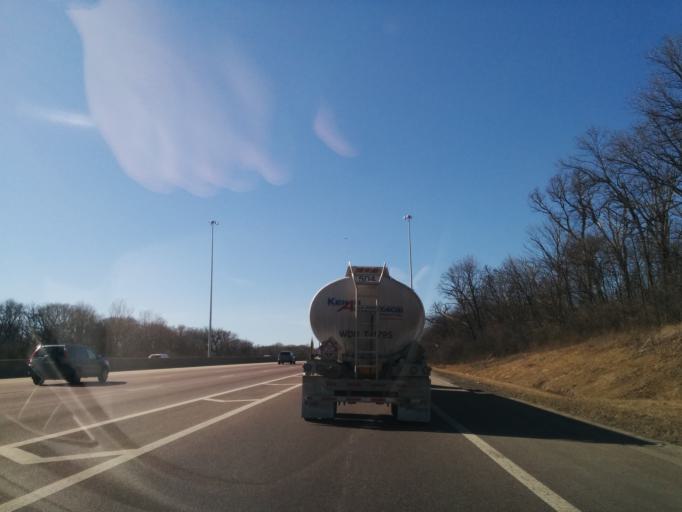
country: US
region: Illinois
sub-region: Cook County
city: Hodgkins
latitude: 41.7610
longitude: -87.8739
